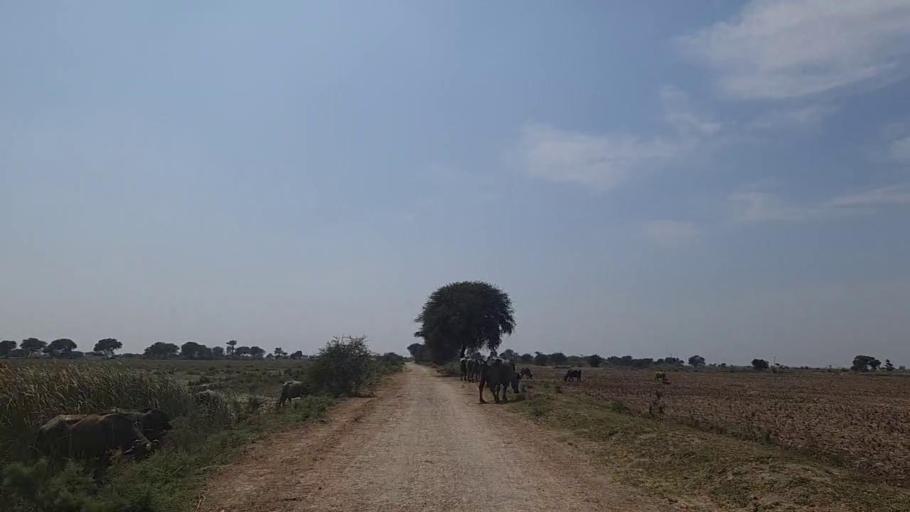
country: PK
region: Sindh
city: Jati
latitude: 24.5357
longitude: 68.3006
